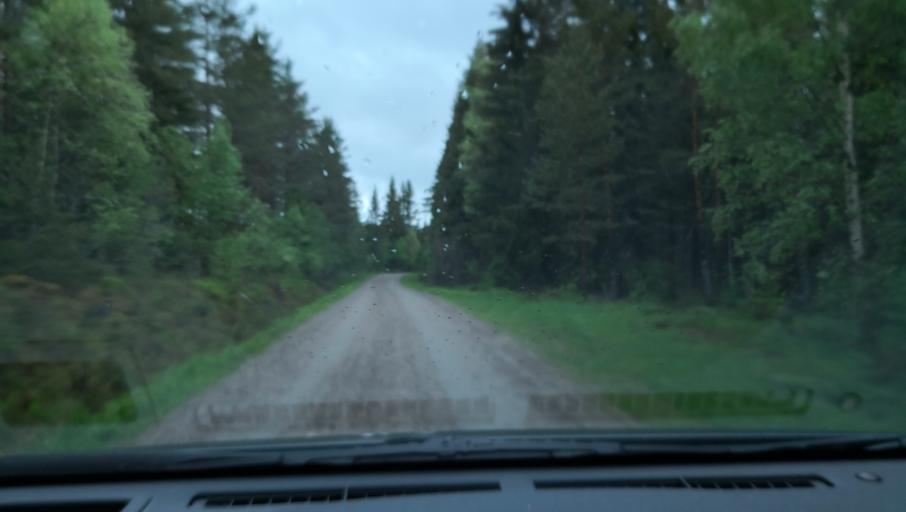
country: SE
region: Uppsala
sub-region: Heby Kommun
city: OEstervala
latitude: 59.9869
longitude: 17.2601
